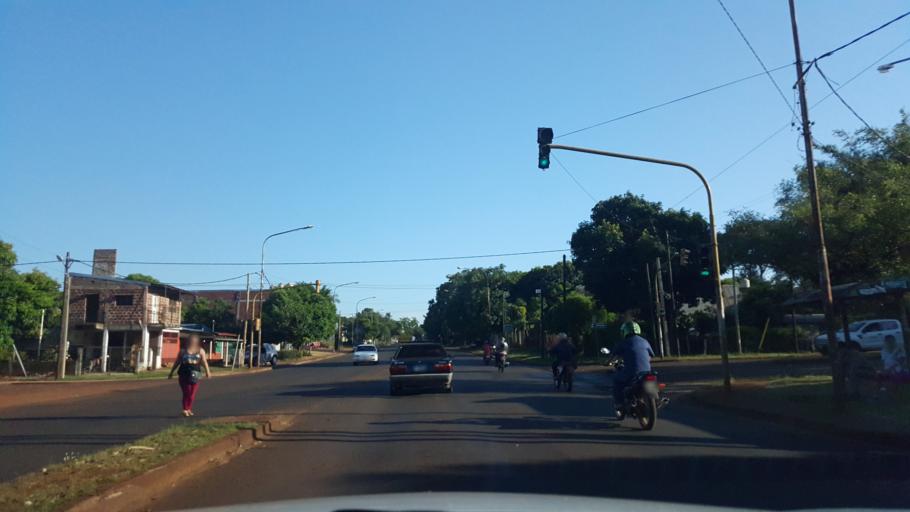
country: AR
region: Misiones
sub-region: Departamento de Capital
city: Posadas
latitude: -27.3926
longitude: -55.9201
